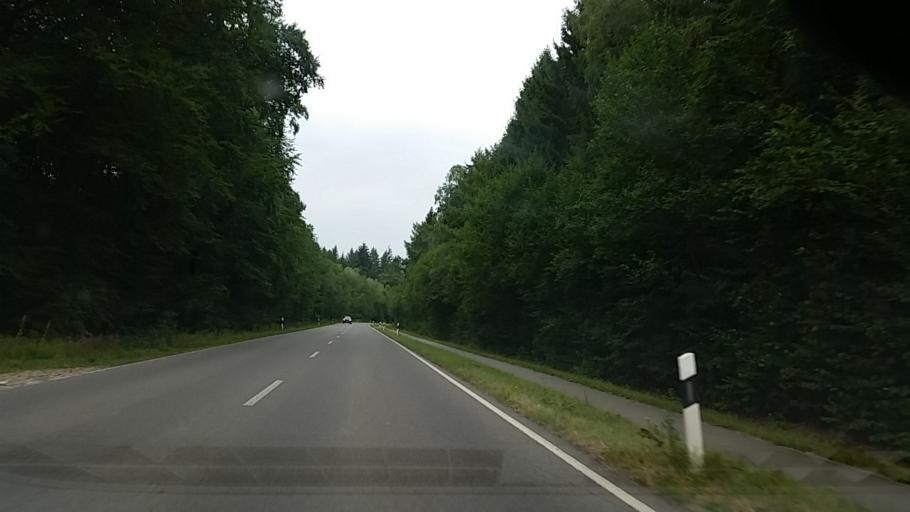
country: DE
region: Schleswig-Holstein
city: Dassendorf
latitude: 53.5121
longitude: 10.3594
